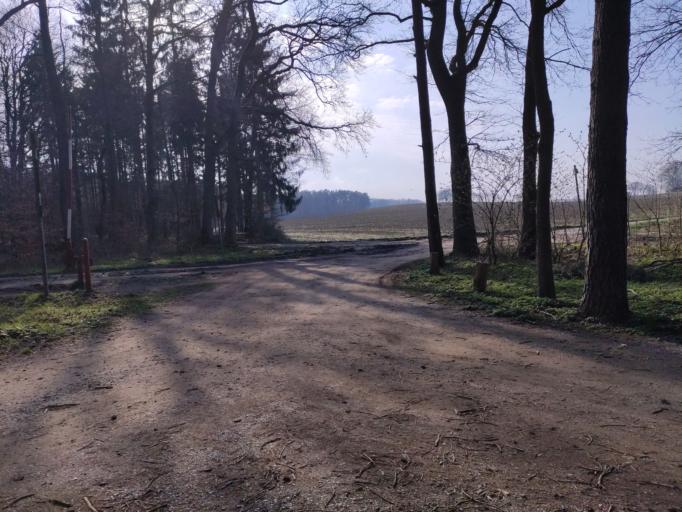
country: DE
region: North Rhine-Westphalia
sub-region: Regierungsbezirk Munster
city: Klein Reken
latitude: 51.7749
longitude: 7.0680
